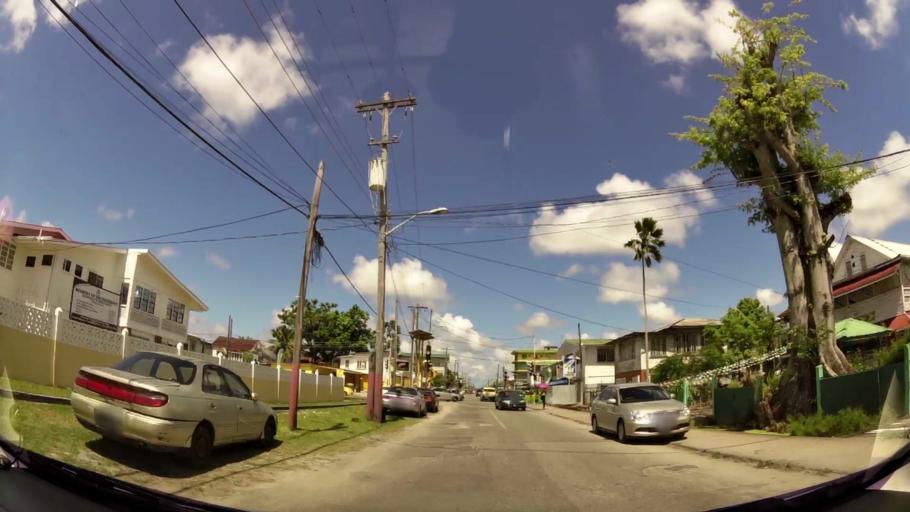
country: GY
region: Demerara-Mahaica
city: Georgetown
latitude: 6.8026
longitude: -58.1514
